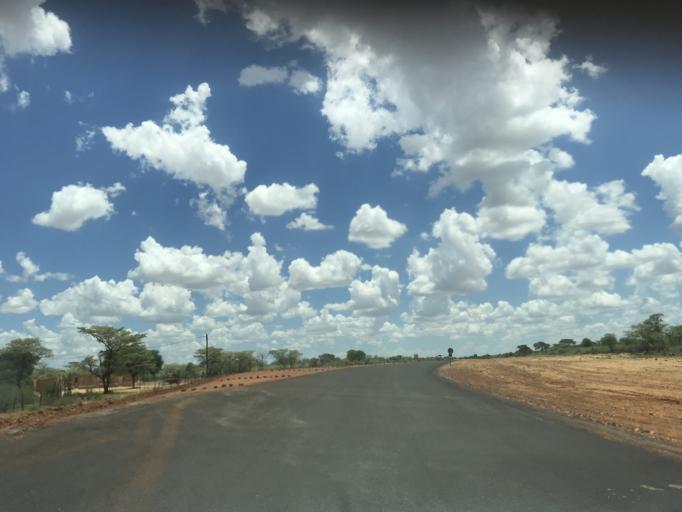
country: BW
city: Mabuli
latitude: -25.8051
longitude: 24.7041
